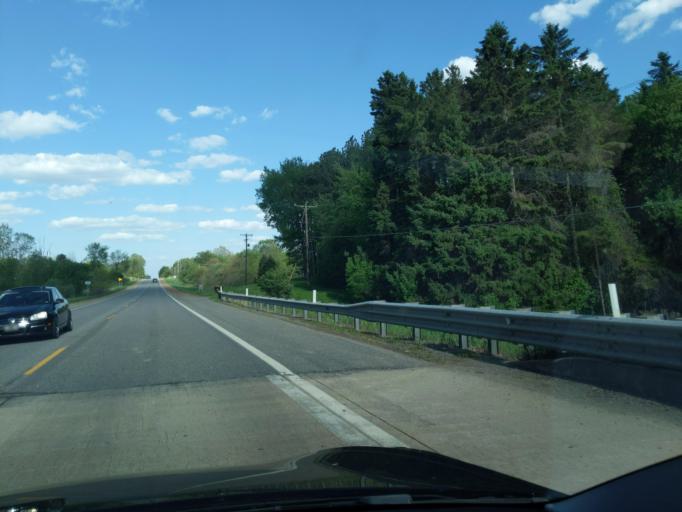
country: US
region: Michigan
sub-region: Ionia County
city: Portland
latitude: 42.7556
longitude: -84.9574
